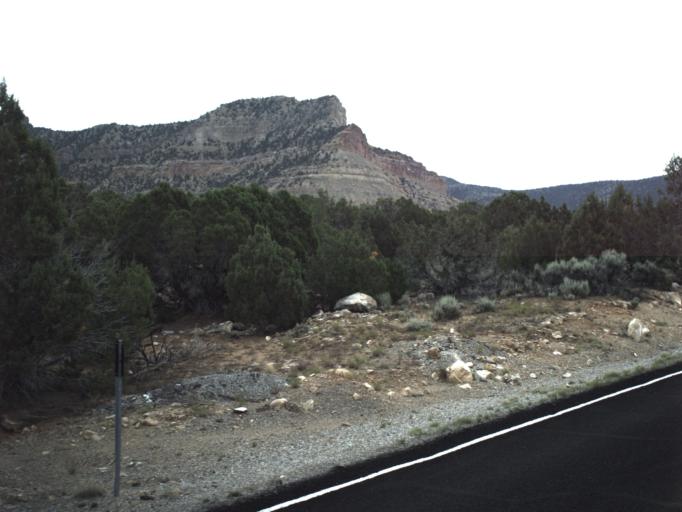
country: US
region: Utah
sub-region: Carbon County
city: East Carbon City
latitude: 39.4632
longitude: -110.3924
